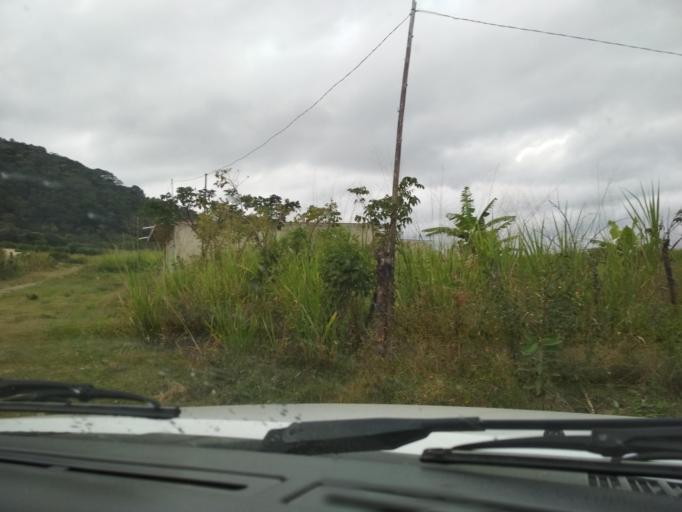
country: MX
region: Veracruz
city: El Castillo
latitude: 19.5696
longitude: -96.8503
